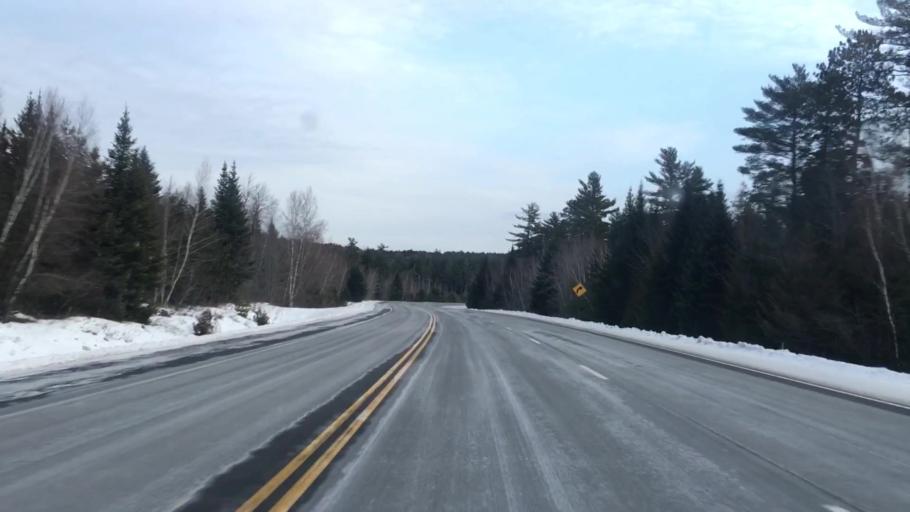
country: US
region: Maine
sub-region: Washington County
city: Addison
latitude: 44.9146
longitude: -67.7910
